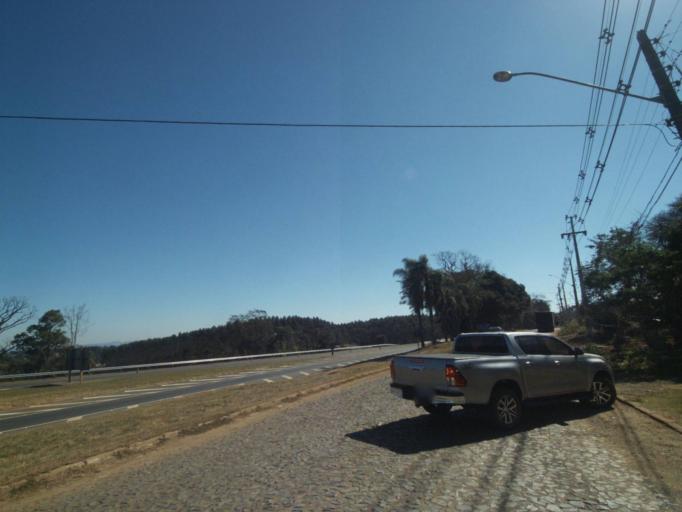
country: BR
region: Parana
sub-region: Reserva
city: Reserva
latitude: -24.6277
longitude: -50.6433
